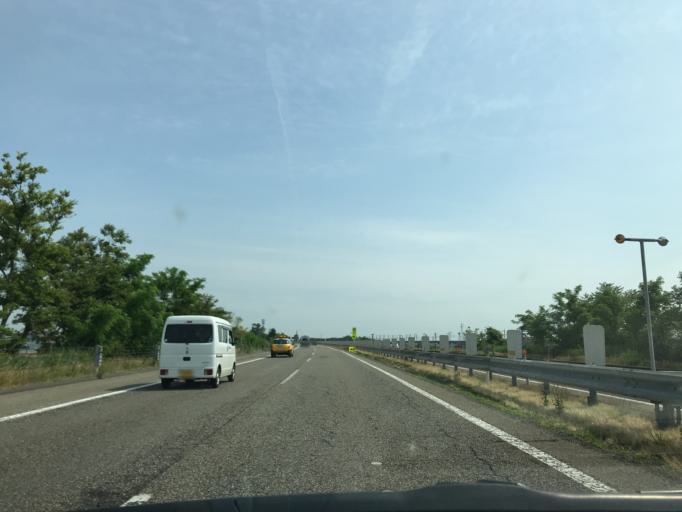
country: JP
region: Niigata
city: Sanjo
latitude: 37.6208
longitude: 138.9234
